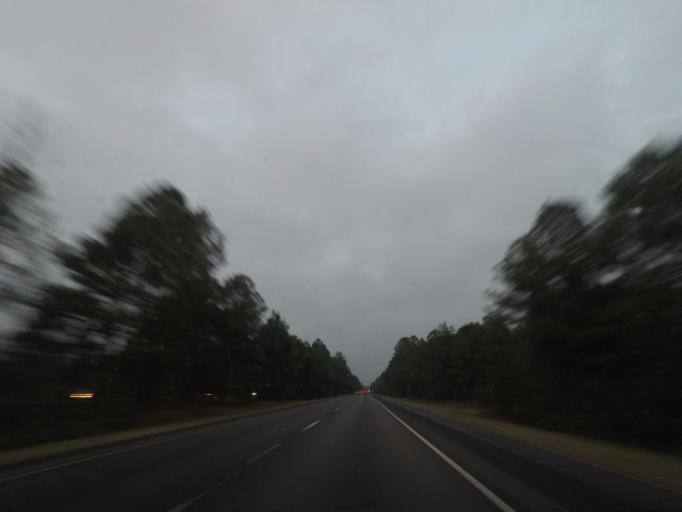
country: US
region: South Carolina
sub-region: Clarendon County
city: Manning
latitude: 33.7817
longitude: -80.1697
